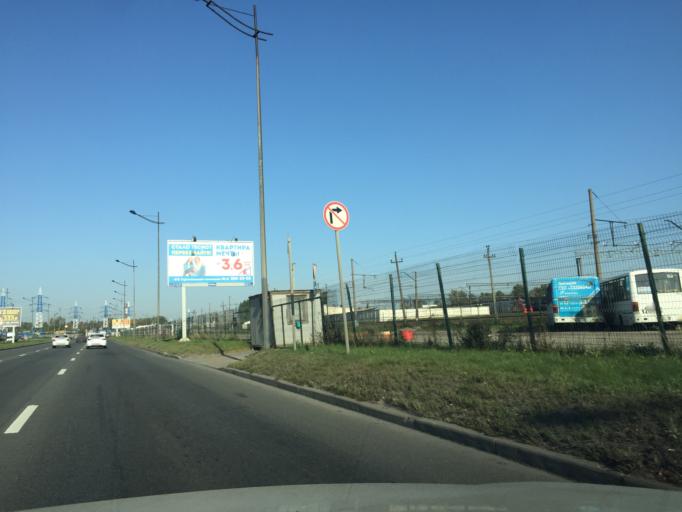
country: RU
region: St.-Petersburg
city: Kupchino
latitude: 59.8833
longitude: 30.3460
